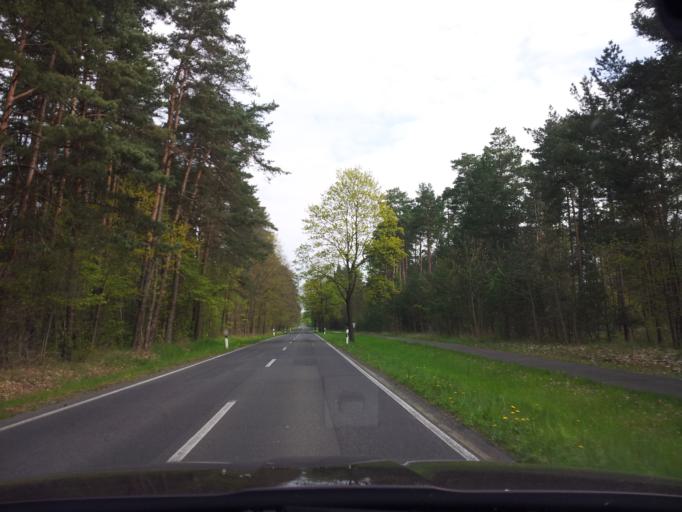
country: DE
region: Brandenburg
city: Rehfelde
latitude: 52.4716
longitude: 13.9078
